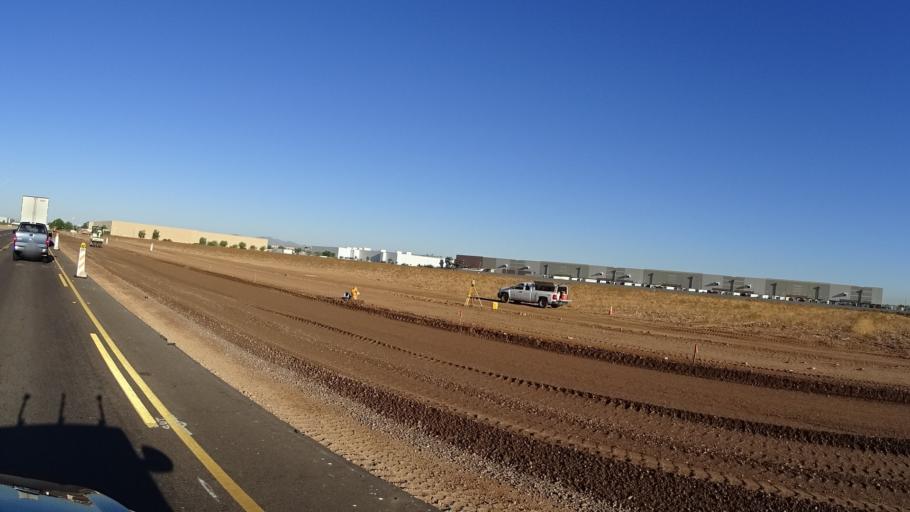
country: US
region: Arizona
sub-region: Maricopa County
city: Tolleson
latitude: 33.4371
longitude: -112.2253
